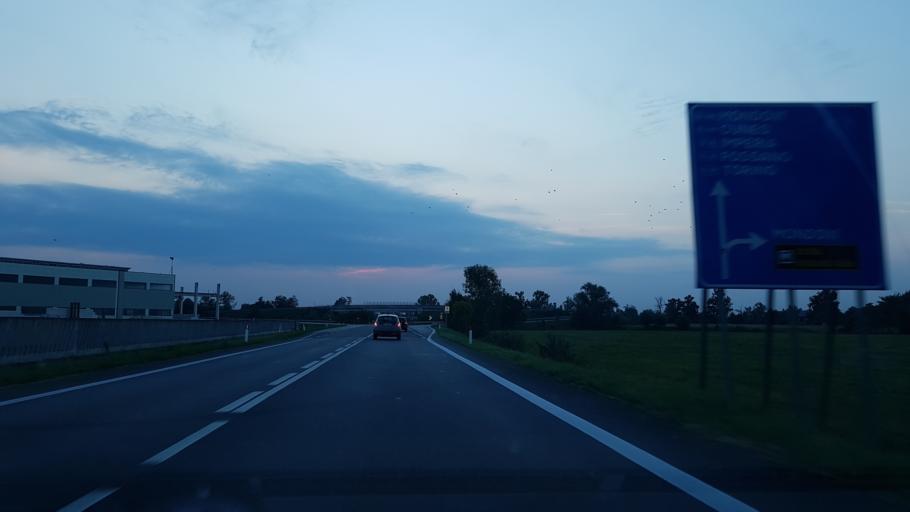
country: IT
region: Piedmont
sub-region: Provincia di Cuneo
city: Breo
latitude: 44.4175
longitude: 7.8209
